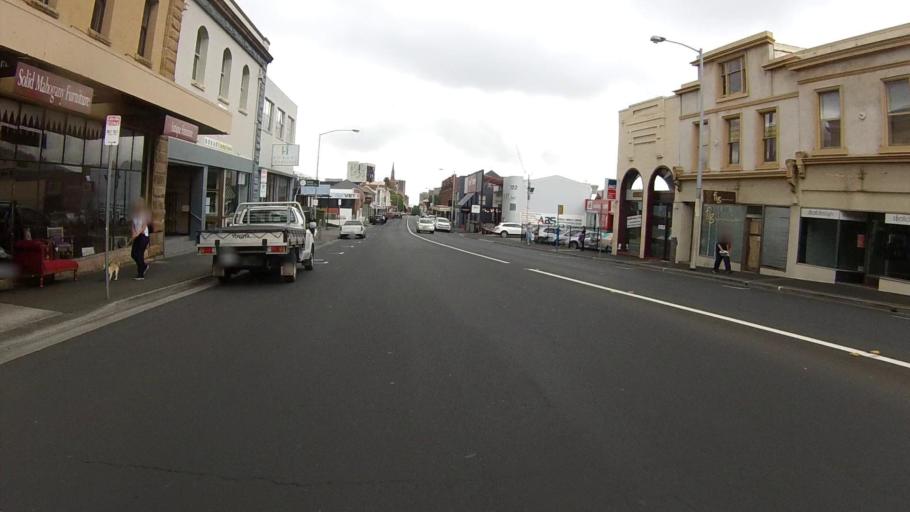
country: AU
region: Tasmania
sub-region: Hobart
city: Hobart
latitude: -42.8779
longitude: 147.3196
